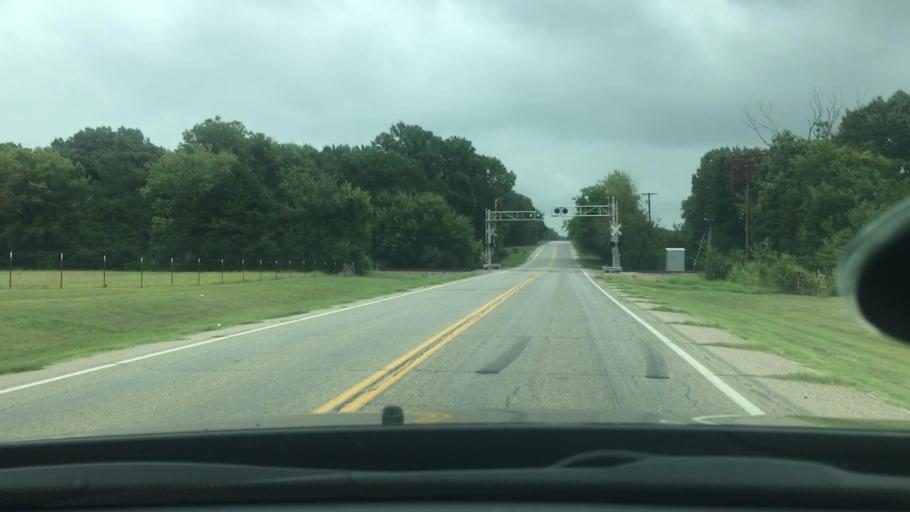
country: US
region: Oklahoma
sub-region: Bryan County
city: Colbert
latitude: 33.8529
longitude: -96.5298
